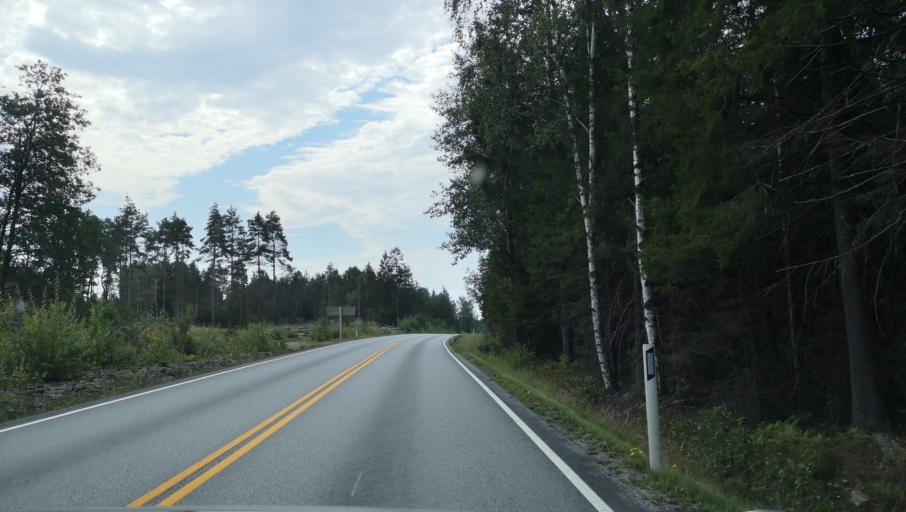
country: NO
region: Ostfold
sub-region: Valer
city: Kirkebygda
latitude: 59.4811
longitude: 10.7943
